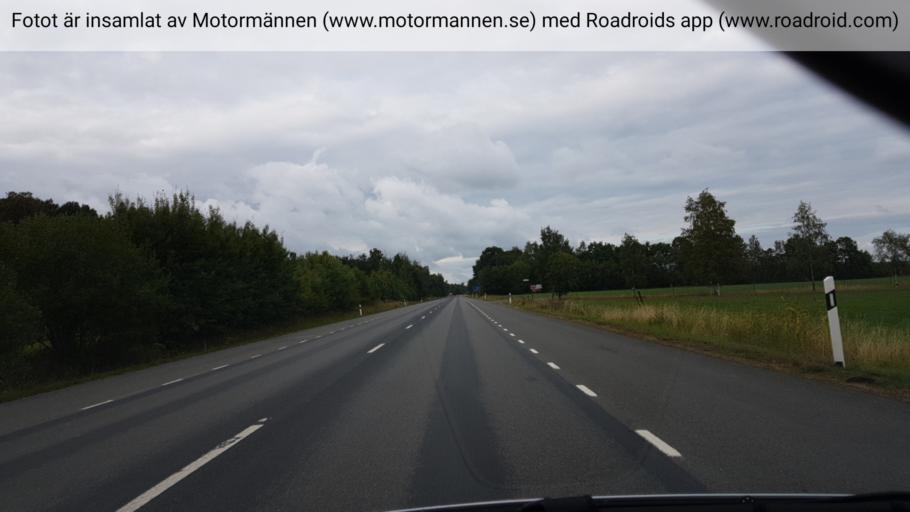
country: SE
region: Vaestra Goetaland
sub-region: Hjo Kommun
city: Hjo
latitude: 58.2830
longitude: 14.2615
